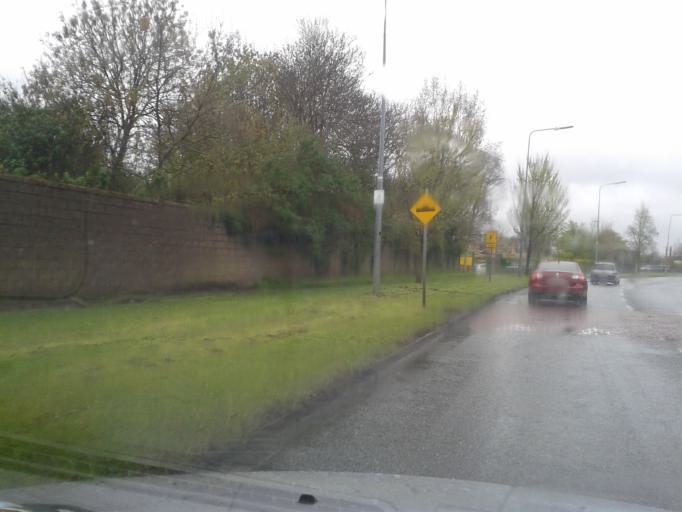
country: IE
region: Leinster
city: Templeogue
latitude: 53.2960
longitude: -6.3241
